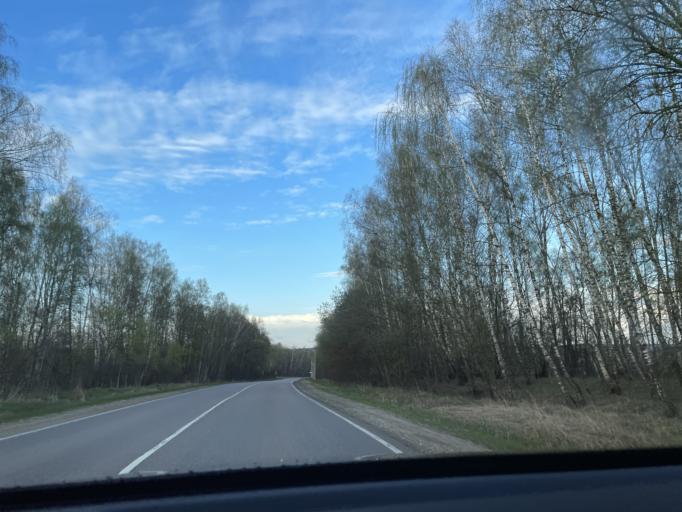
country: RU
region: Tula
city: Novogurovskiy
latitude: 54.5204
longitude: 37.2485
